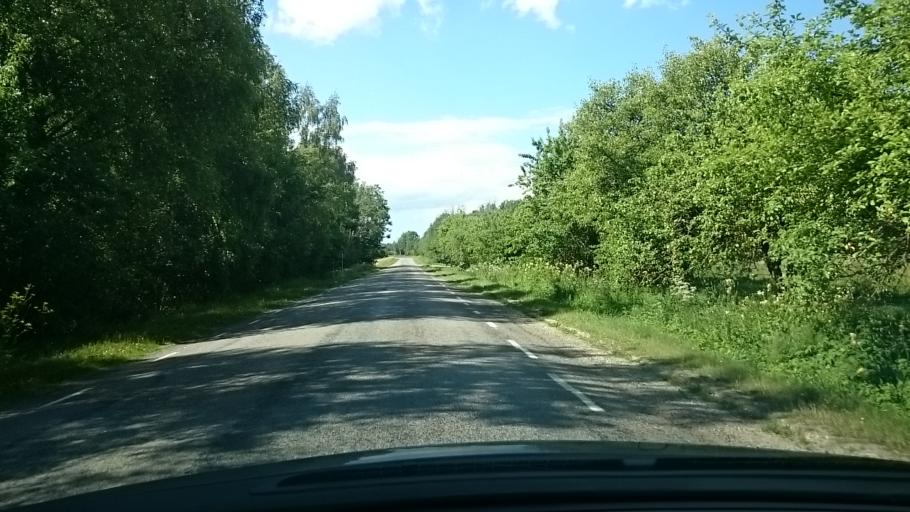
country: EE
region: Laeaene
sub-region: Ridala Parish
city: Uuemoisa
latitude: 59.0686
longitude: 23.5825
